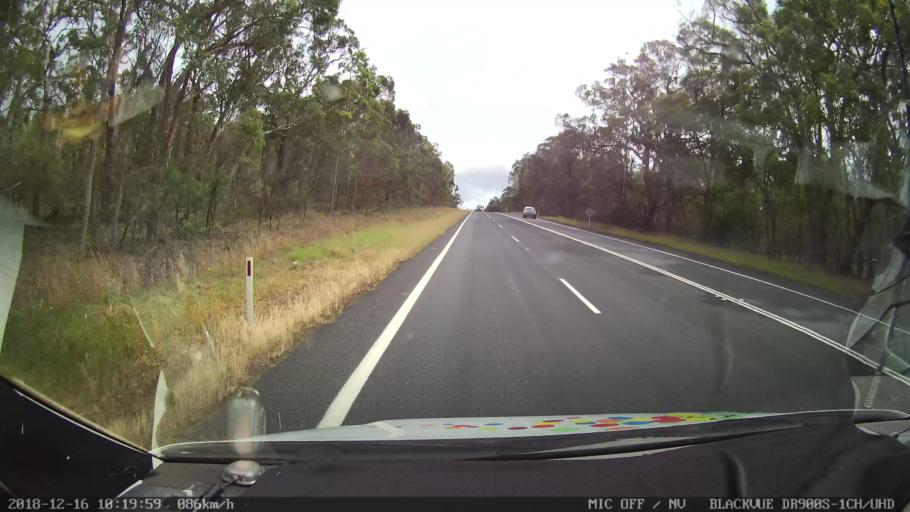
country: AU
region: New South Wales
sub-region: Tenterfield Municipality
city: Carrolls Creek
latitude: -29.2260
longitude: 152.0091
